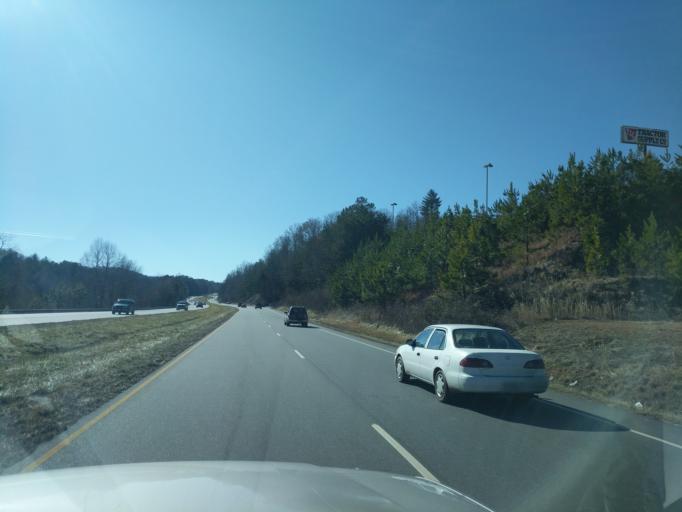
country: US
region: North Carolina
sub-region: Cherokee County
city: Murphy
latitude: 35.0548
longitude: -84.0689
